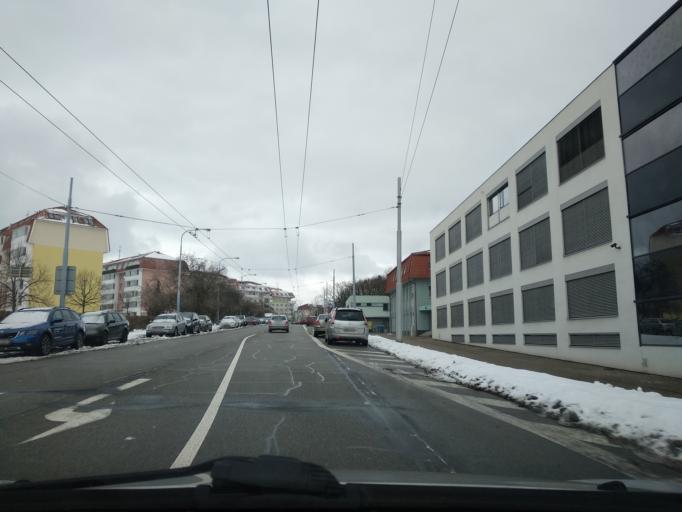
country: CZ
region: South Moravian
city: Troubsko
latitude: 49.1886
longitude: 16.5330
